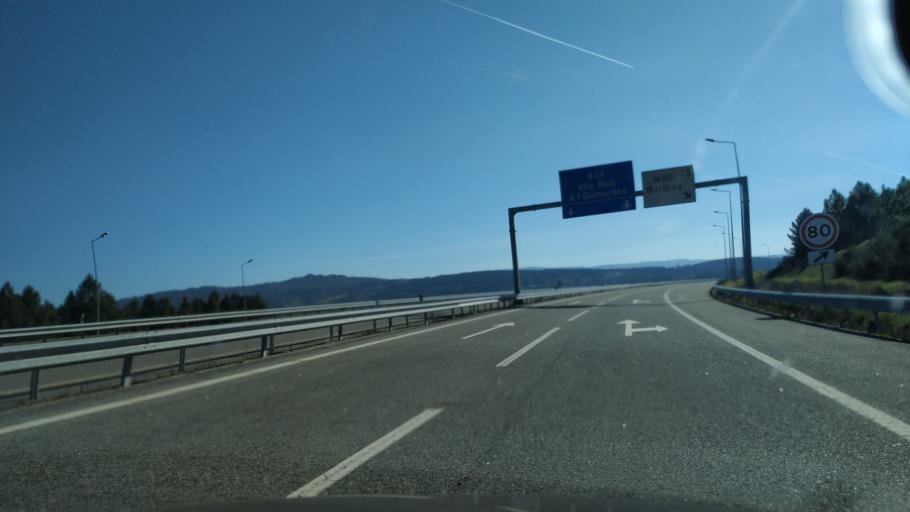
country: PT
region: Vila Real
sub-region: Chaves
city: Chaves
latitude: 41.7167
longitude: -7.5429
